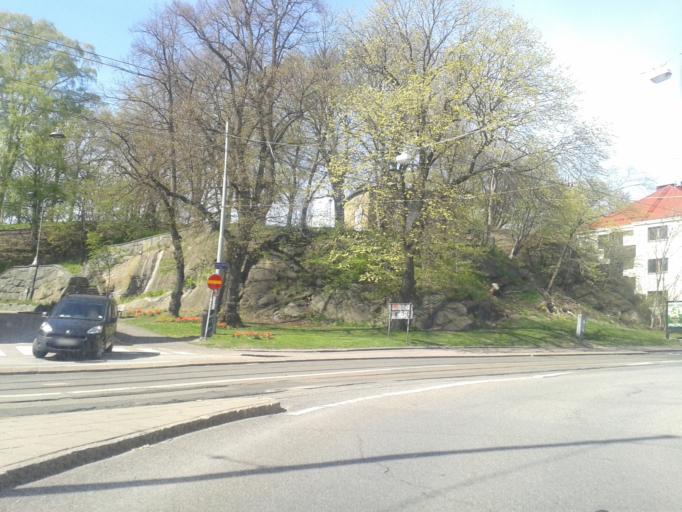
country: SE
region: Vaestra Goetaland
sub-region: Goteborg
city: Goeteborg
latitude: 57.7169
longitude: 12.0051
